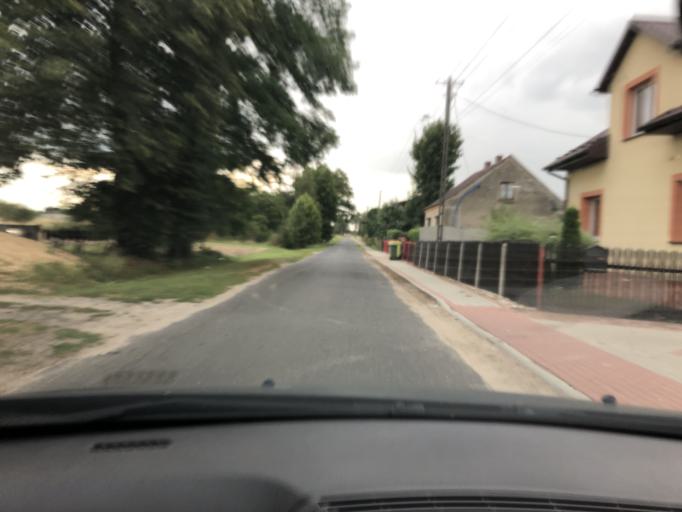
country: PL
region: Lodz Voivodeship
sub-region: Powiat wieruszowski
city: Czastary
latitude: 51.2403
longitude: 18.2932
